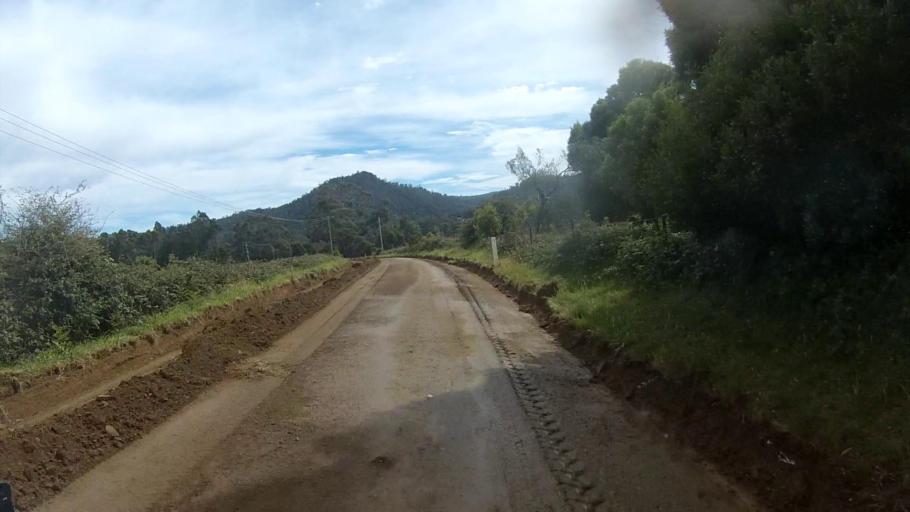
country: AU
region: Tasmania
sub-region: Sorell
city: Sorell
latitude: -42.7750
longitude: 147.8088
